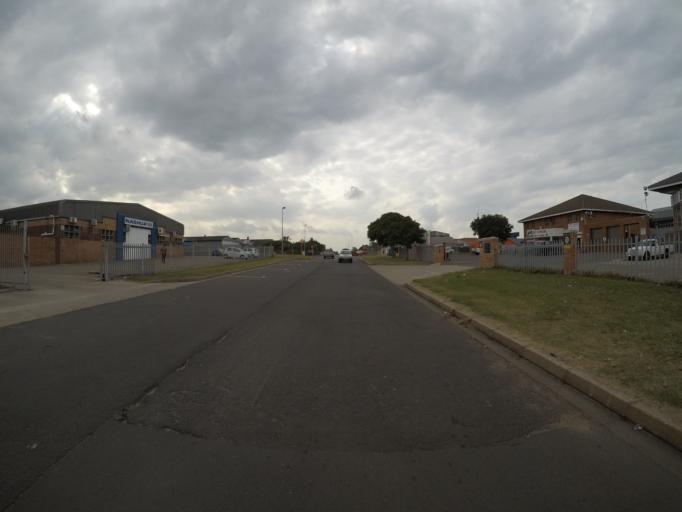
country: ZA
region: KwaZulu-Natal
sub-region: uThungulu District Municipality
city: Richards Bay
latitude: -28.7573
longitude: 32.0427
